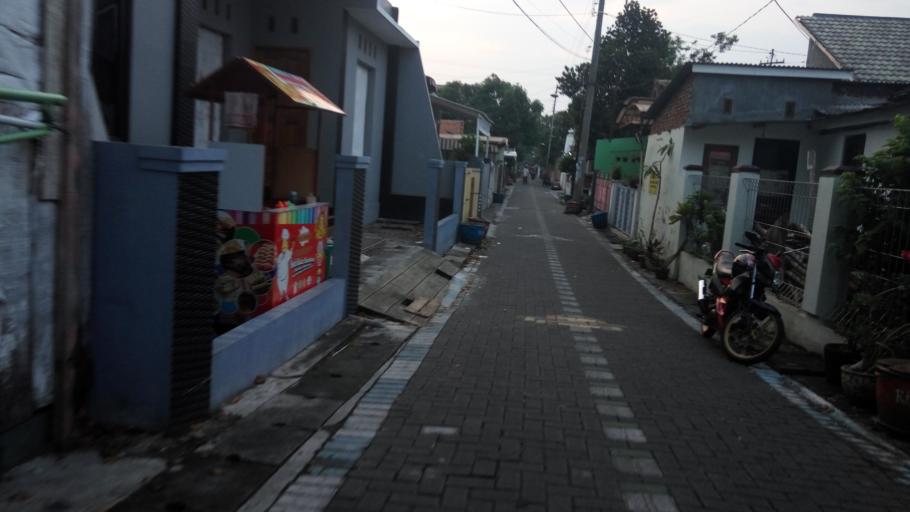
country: ID
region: Central Java
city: Semarang
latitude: -6.9866
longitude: 110.4051
